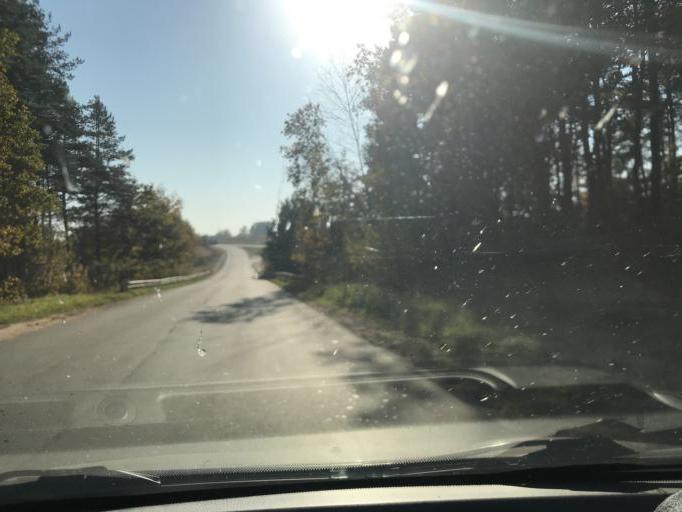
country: BY
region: Minsk
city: Pryvol'ny
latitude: 53.7927
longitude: 27.7425
